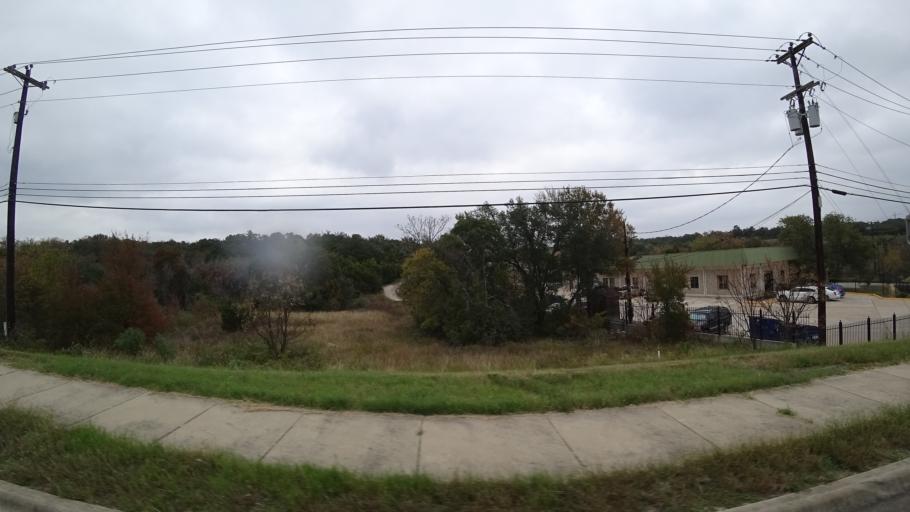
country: US
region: Texas
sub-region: Williamson County
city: Anderson Mill
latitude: 30.4606
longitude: -97.8400
